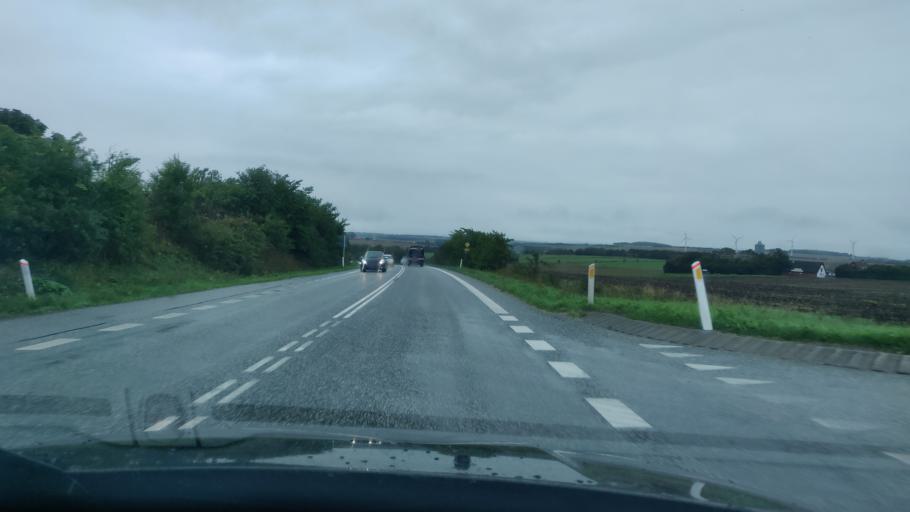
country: DK
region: North Denmark
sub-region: Thisted Kommune
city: Thisted
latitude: 56.9747
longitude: 8.7520
